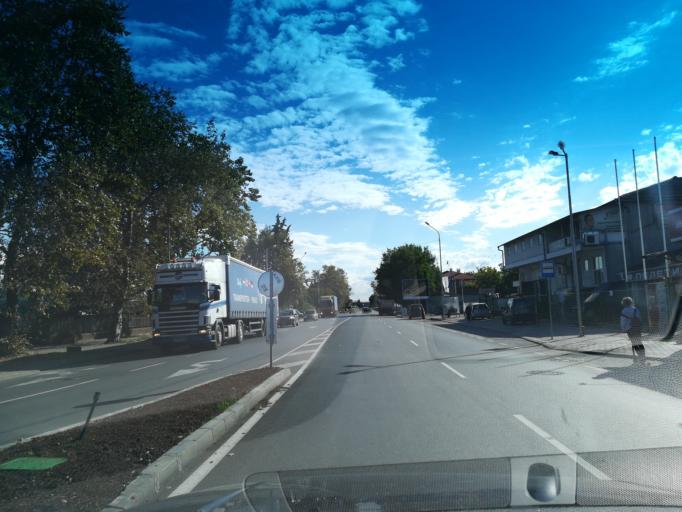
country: BG
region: Stara Zagora
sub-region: Obshtina Stara Zagora
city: Stara Zagora
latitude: 42.3984
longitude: 25.6444
